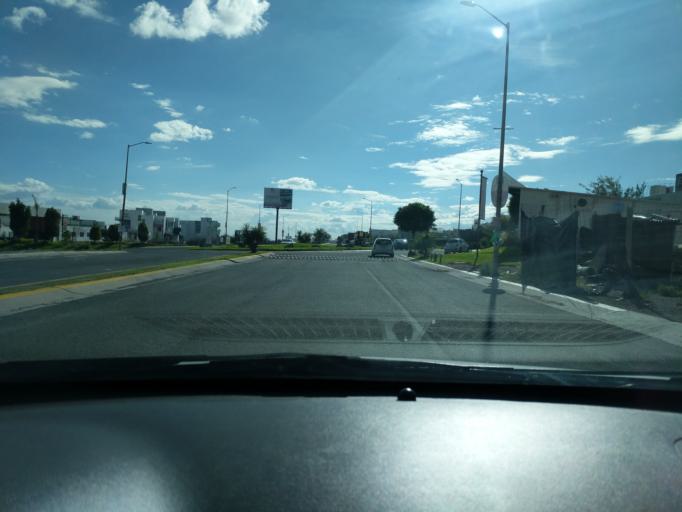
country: MX
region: Queretaro
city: La Canada
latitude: 20.5923
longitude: -100.3253
